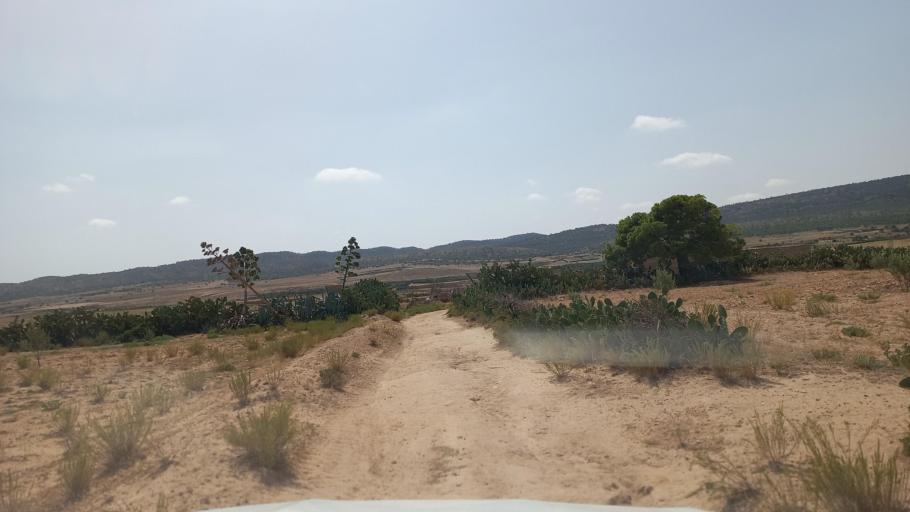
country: TN
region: Al Qasrayn
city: Sbiba
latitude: 35.3951
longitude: 8.9591
